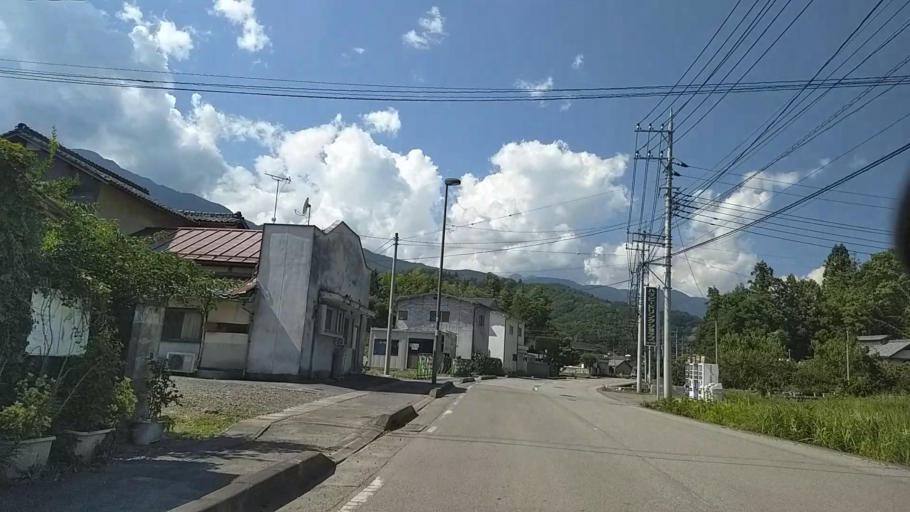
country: JP
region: Yamanashi
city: Ryuo
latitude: 35.4616
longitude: 138.4449
